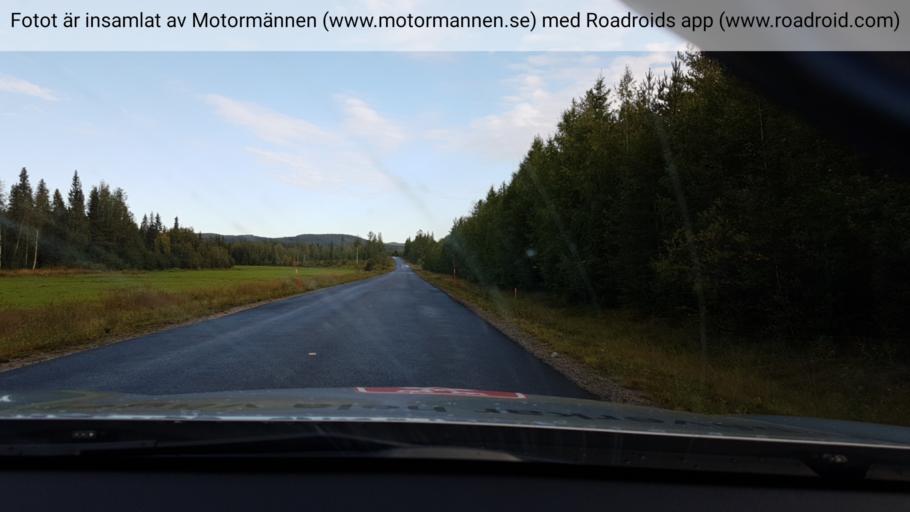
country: SE
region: Vaesterbotten
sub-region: Vindelns Kommun
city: Vindeln
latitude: 64.2126
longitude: 19.7644
